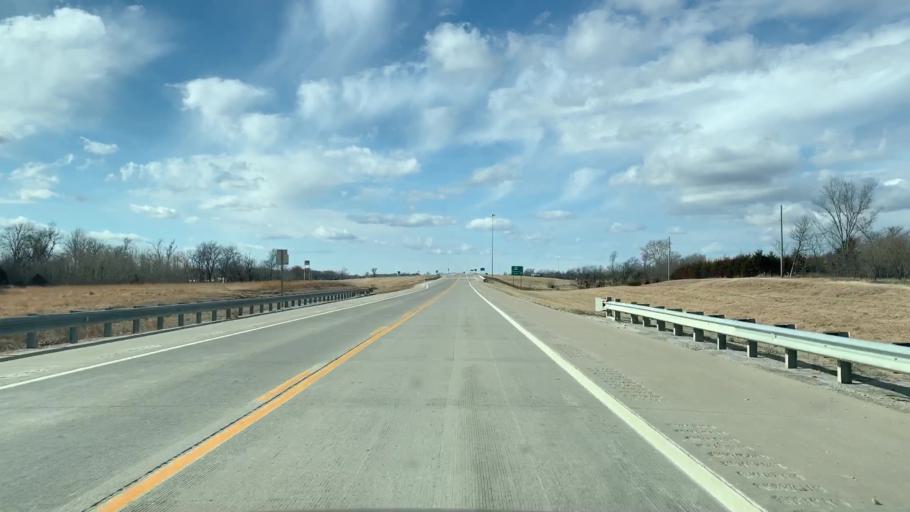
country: US
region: Kansas
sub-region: Labette County
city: Parsons
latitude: 37.3653
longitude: -95.2496
